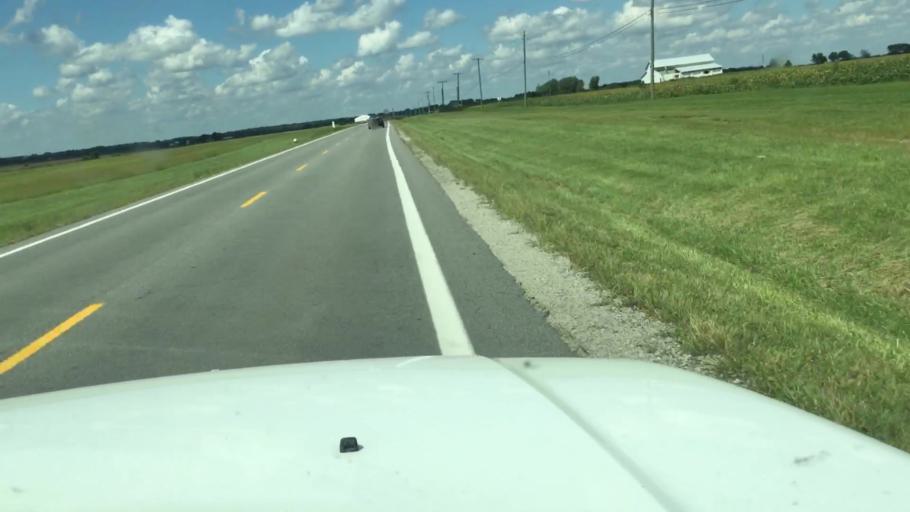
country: US
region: Ohio
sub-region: Madison County
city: London
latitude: 39.9141
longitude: -83.4779
